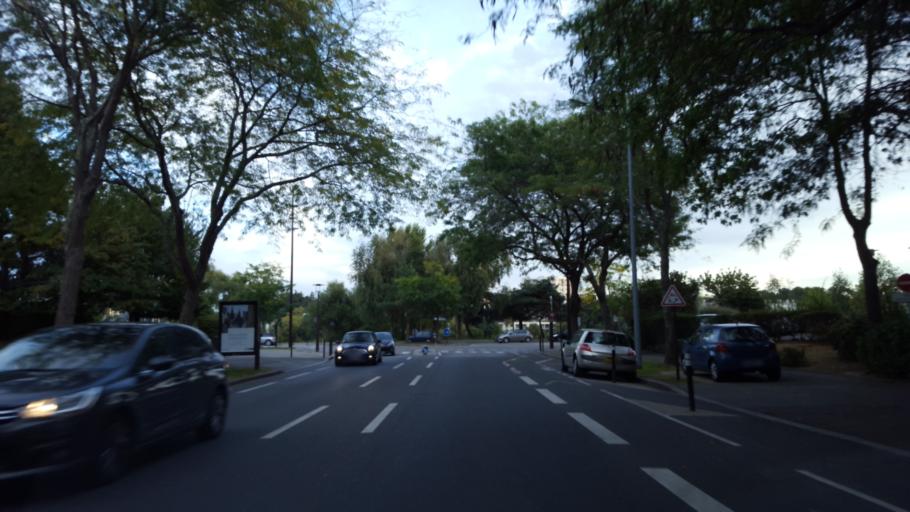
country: FR
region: Pays de la Loire
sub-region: Departement de la Loire-Atlantique
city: Saint-Sebastien-sur-Loire
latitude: 47.2066
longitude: -1.5290
